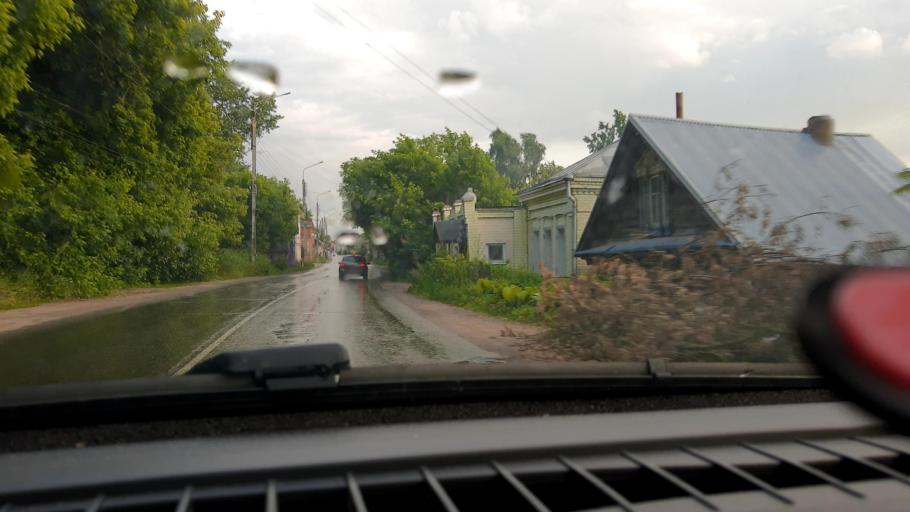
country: RU
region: Nizjnij Novgorod
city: Gorodets
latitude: 56.6489
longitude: 43.4651
